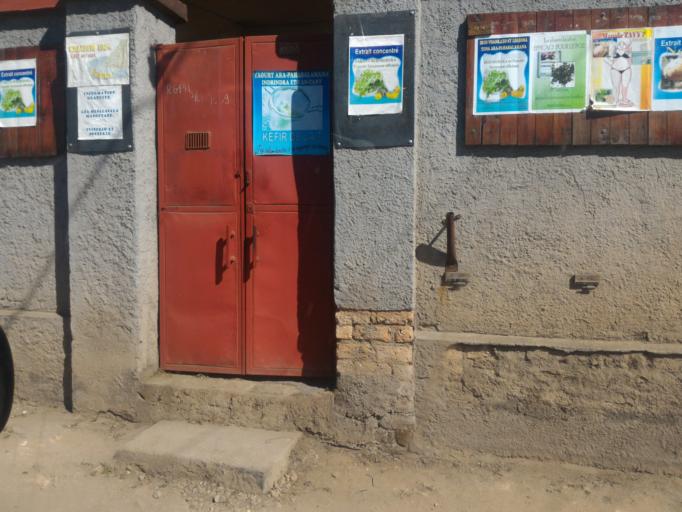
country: MG
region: Analamanga
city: Antananarivo
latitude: -18.9152
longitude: 47.5377
